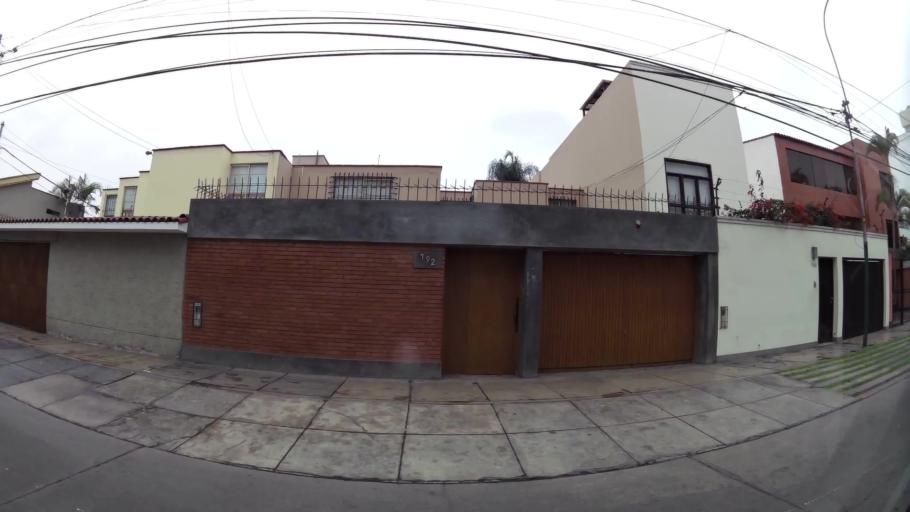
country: PE
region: Lima
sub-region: Lima
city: Surco
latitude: -12.1326
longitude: -77.0075
